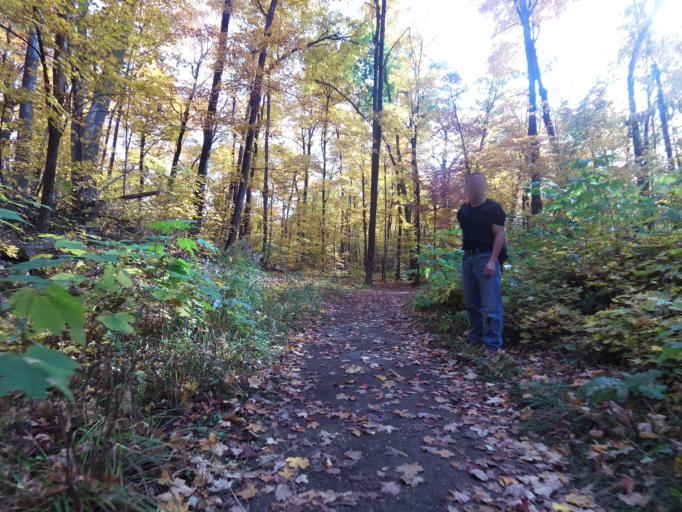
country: CA
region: Quebec
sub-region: Outaouais
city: Gatineau
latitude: 45.4725
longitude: -75.8174
